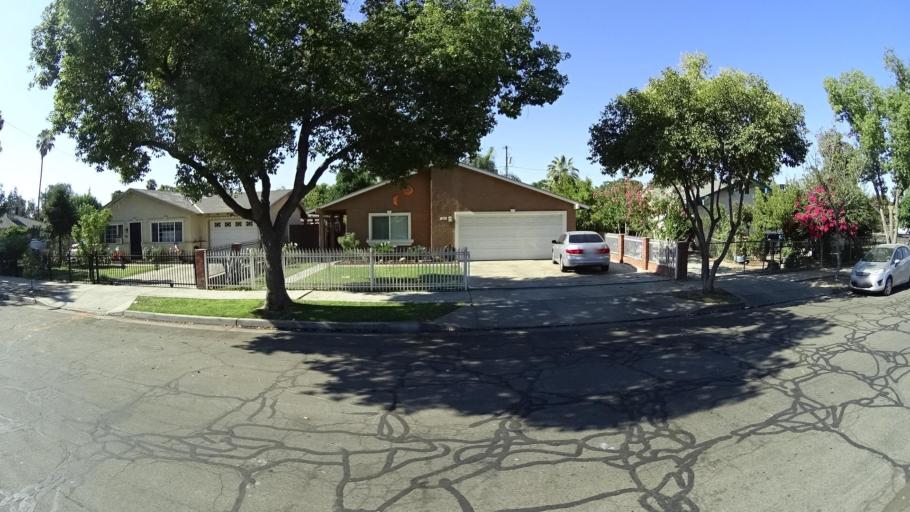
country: US
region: California
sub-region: Fresno County
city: Fresno
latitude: 36.7307
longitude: -119.7653
